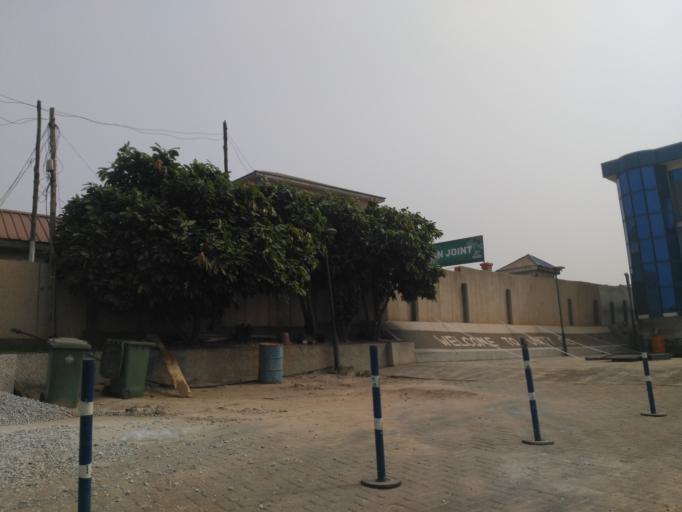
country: GH
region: Ashanti
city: Kumasi
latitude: 6.6740
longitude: -1.6402
